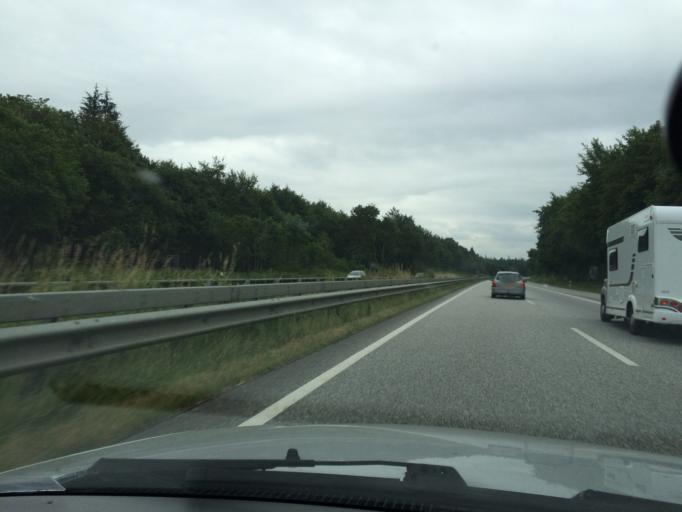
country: DE
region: Schleswig-Holstein
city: Handewitt
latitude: 54.7590
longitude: 9.3640
